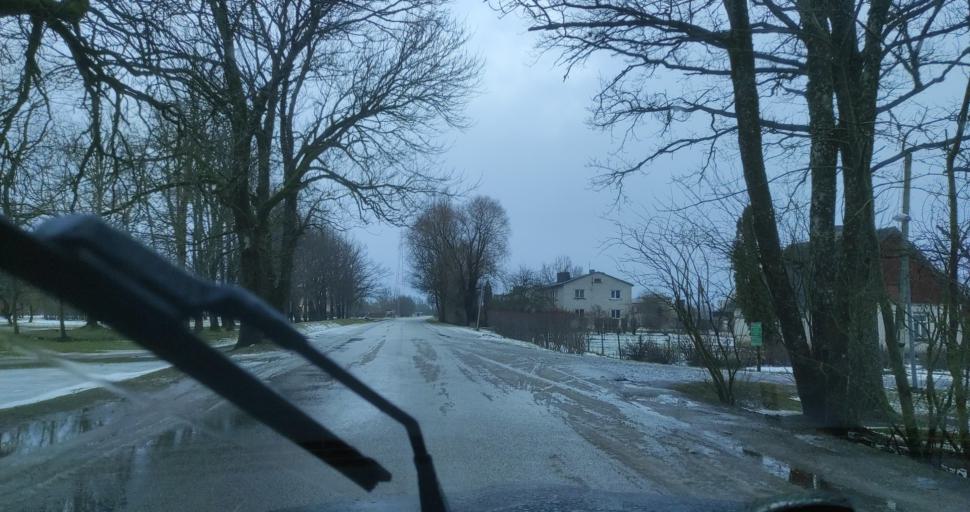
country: LV
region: Dundaga
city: Dundaga
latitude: 57.5141
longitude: 22.0212
